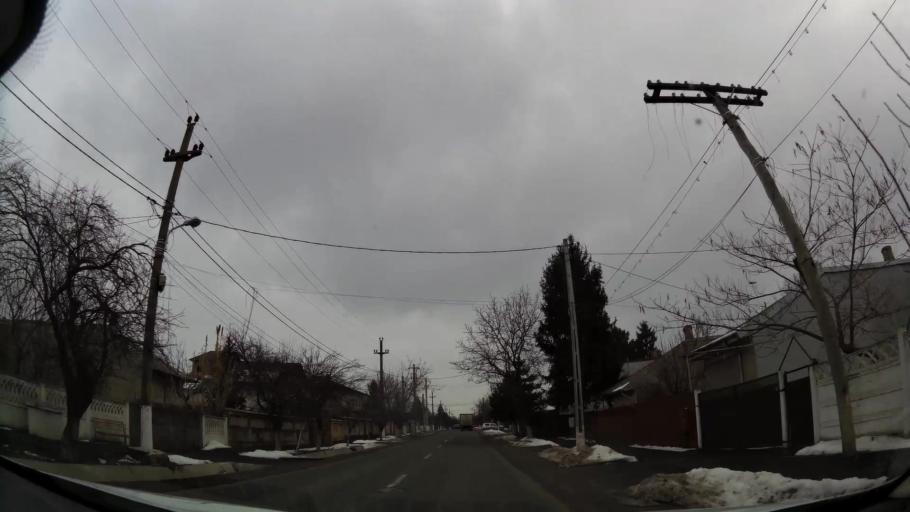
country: RO
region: Ilfov
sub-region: Comuna Afumati
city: Afumati
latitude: 44.5262
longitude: 26.2445
